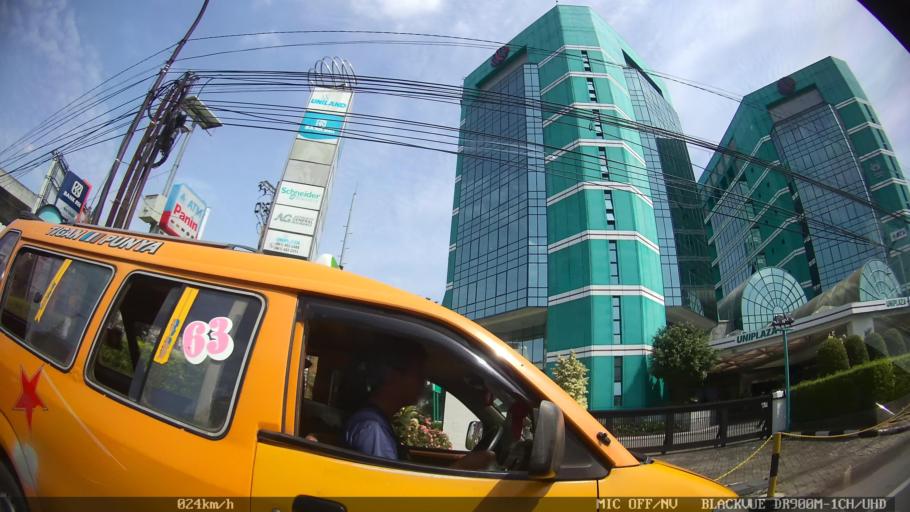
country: ID
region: North Sumatra
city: Medan
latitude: 3.5857
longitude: 98.6823
